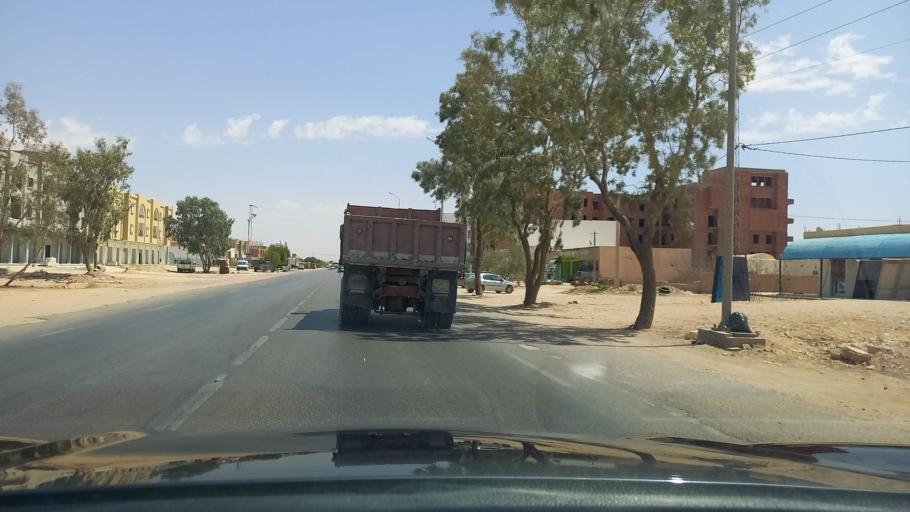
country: TN
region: Madanin
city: Medenine
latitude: 33.3659
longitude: 10.4578
